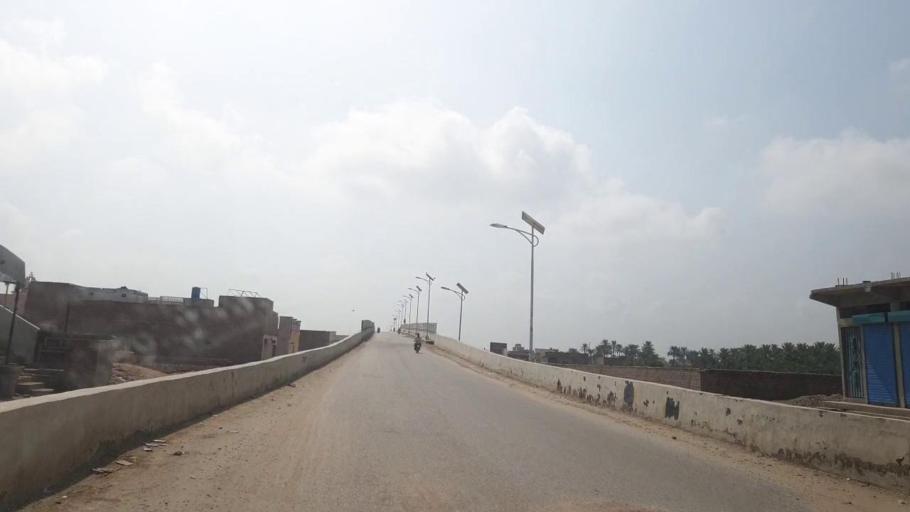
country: PK
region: Sindh
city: Khairpur
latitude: 27.5305
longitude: 68.7380
